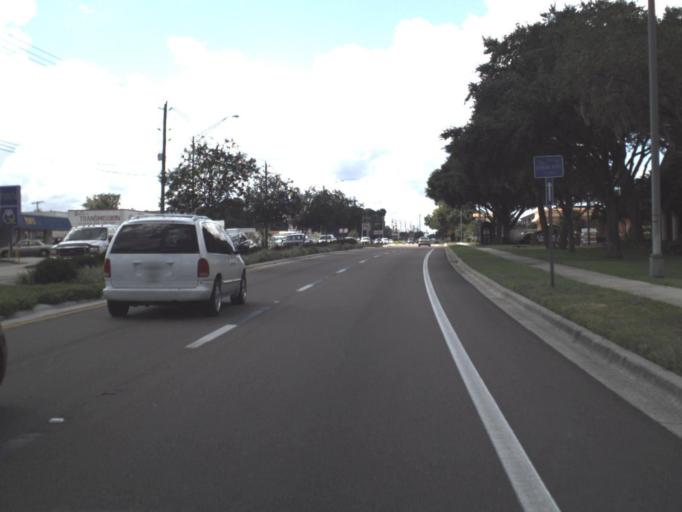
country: US
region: Florida
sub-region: Polk County
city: Lakeland
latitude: 28.0692
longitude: -81.9575
